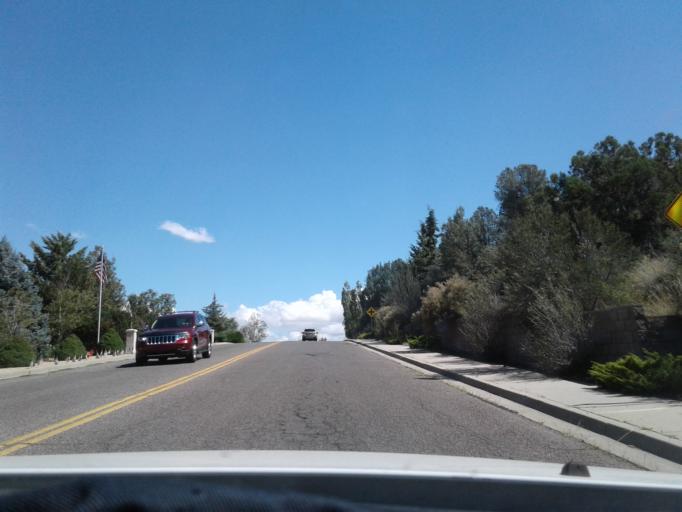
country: US
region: Arizona
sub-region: Yavapai County
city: Prescott
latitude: 34.5693
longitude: -112.4636
